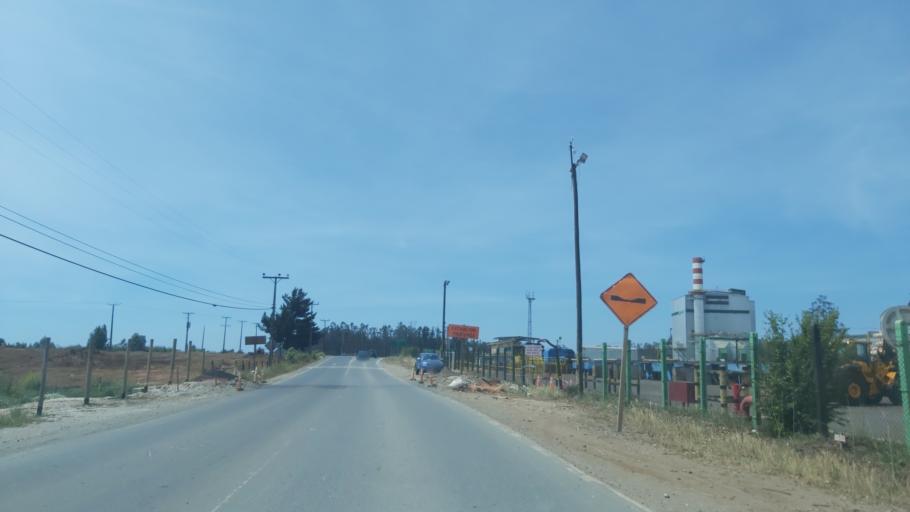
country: CL
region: Maule
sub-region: Provincia de Talca
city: Constitucion
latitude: -35.3728
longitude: -72.4141
